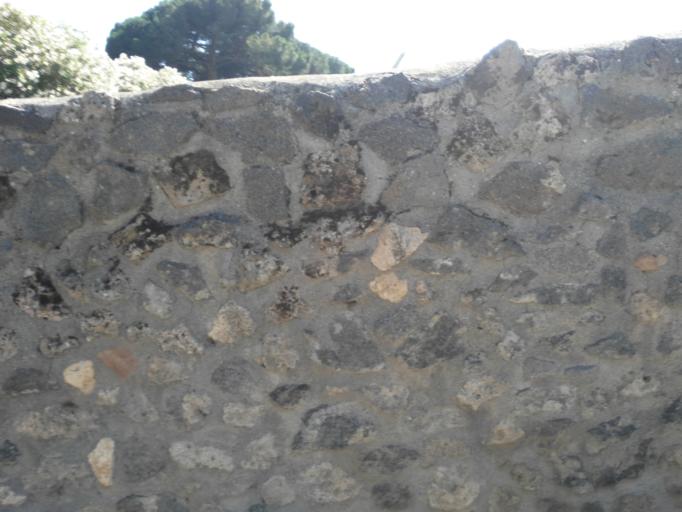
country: IT
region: Campania
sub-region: Provincia di Napoli
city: Pompei
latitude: 40.7492
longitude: 14.4926
